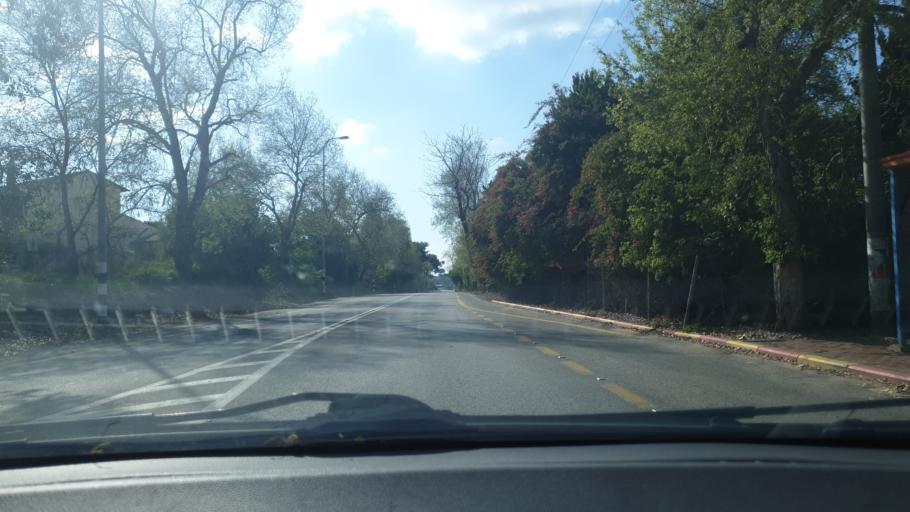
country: IL
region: Central District
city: Bet Yizhaq
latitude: 32.3440
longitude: 34.9148
